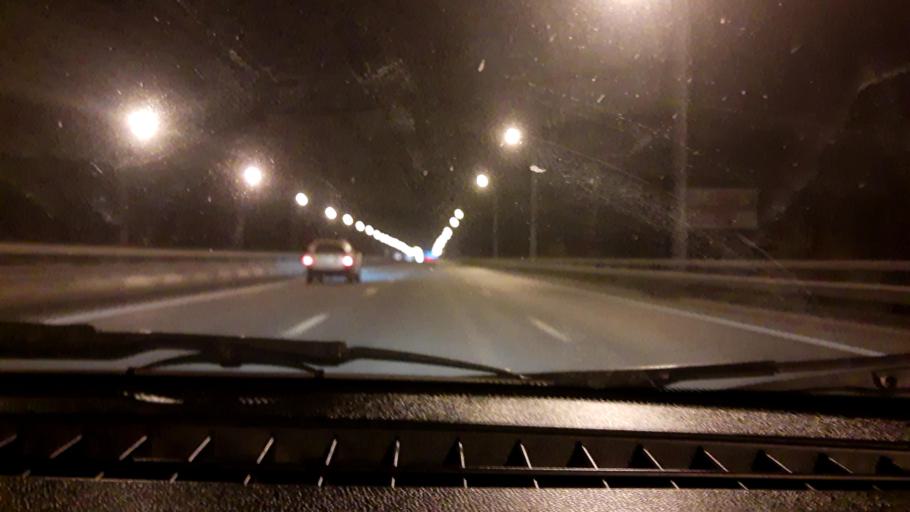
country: RU
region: Bashkortostan
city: Ufa
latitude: 54.6436
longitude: 55.9734
